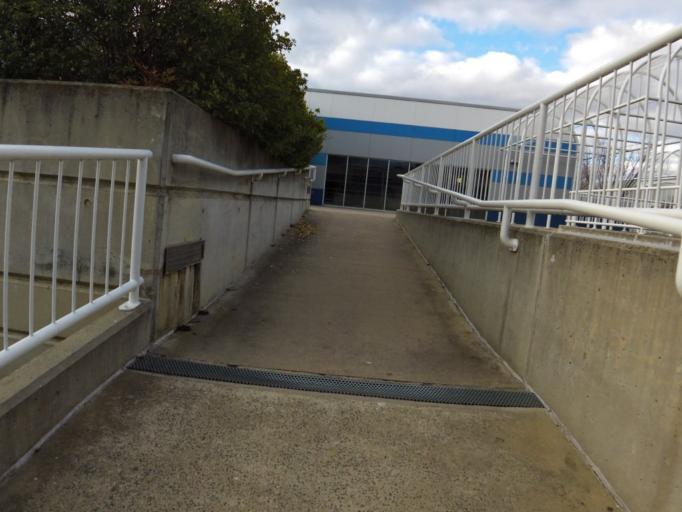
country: AU
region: Australian Capital Territory
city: Kaleen
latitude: -35.2469
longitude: 149.1024
